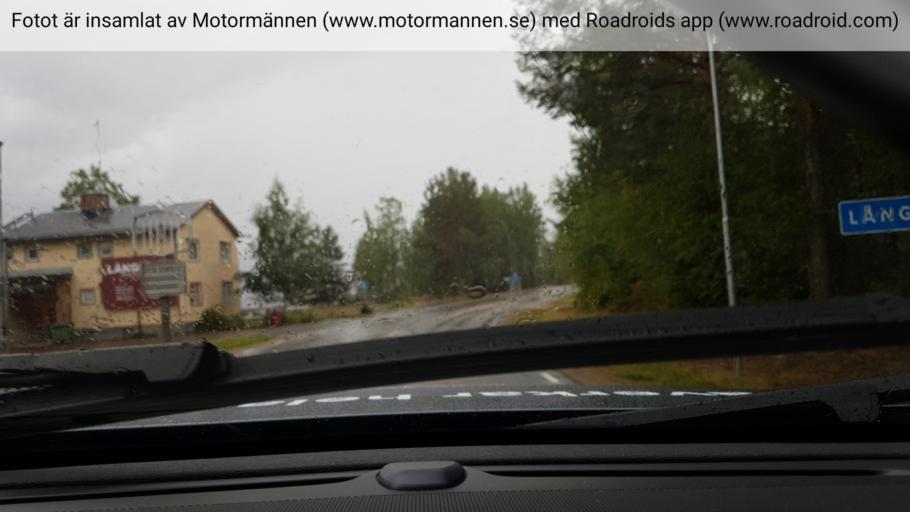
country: NO
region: Hedmark
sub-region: Trysil
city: Innbygda
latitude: 61.0465
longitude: 12.5962
